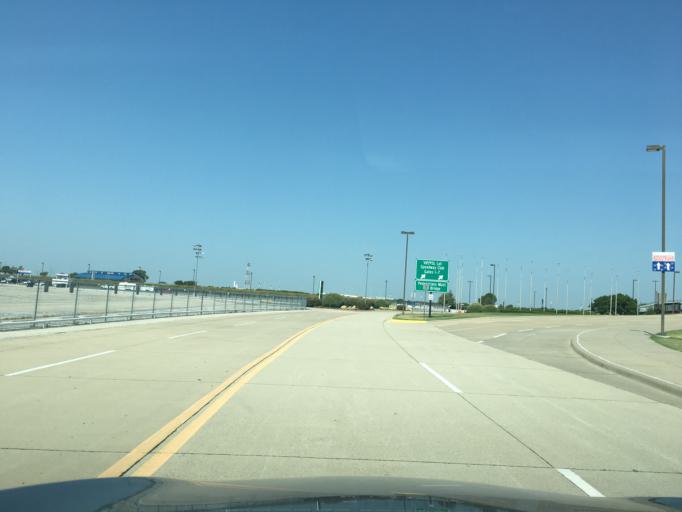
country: US
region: Texas
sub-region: Denton County
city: Justin
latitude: 33.0307
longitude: -97.2820
